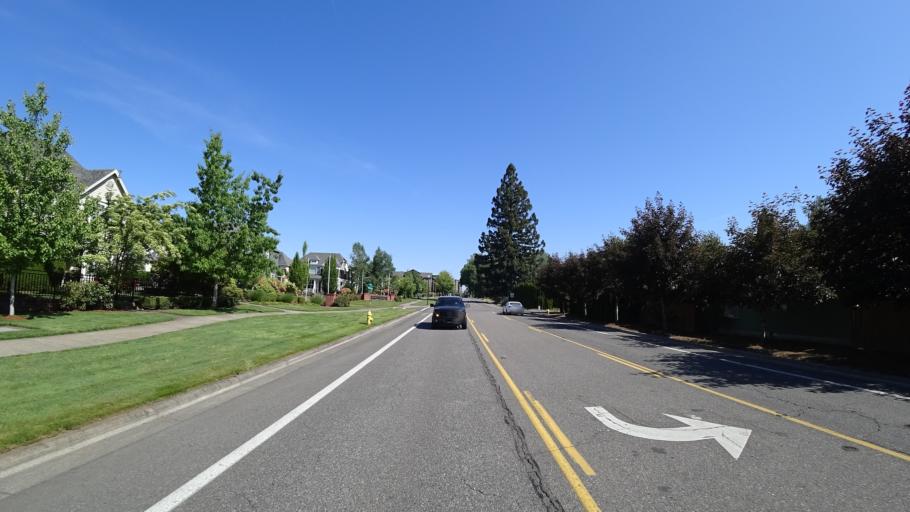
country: US
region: Oregon
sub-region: Washington County
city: Rockcreek
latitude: 45.5272
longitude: -122.9148
